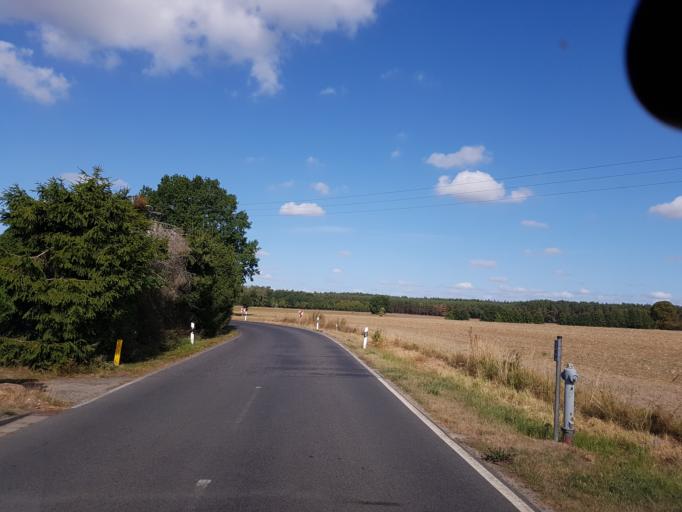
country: DE
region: Brandenburg
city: Sonnewalde
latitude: 51.7348
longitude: 13.6304
